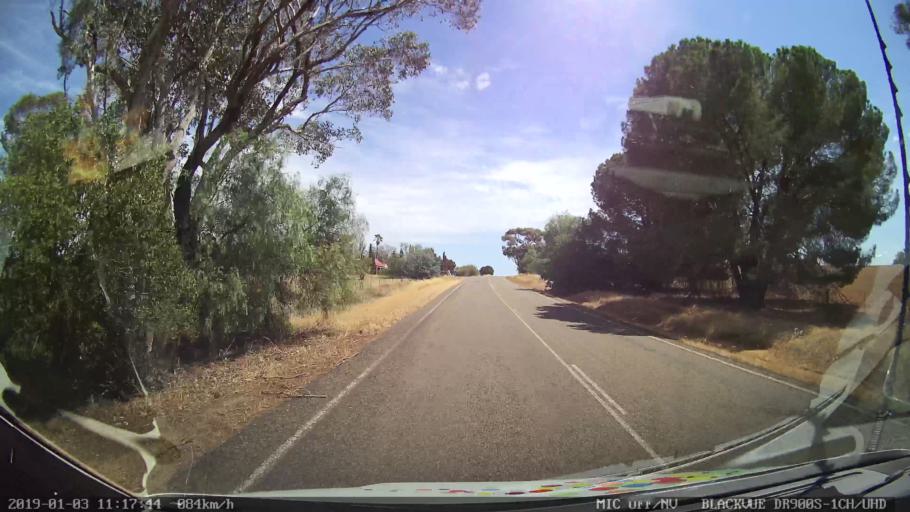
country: AU
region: New South Wales
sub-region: Young
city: Young
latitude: -34.1350
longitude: 148.2647
